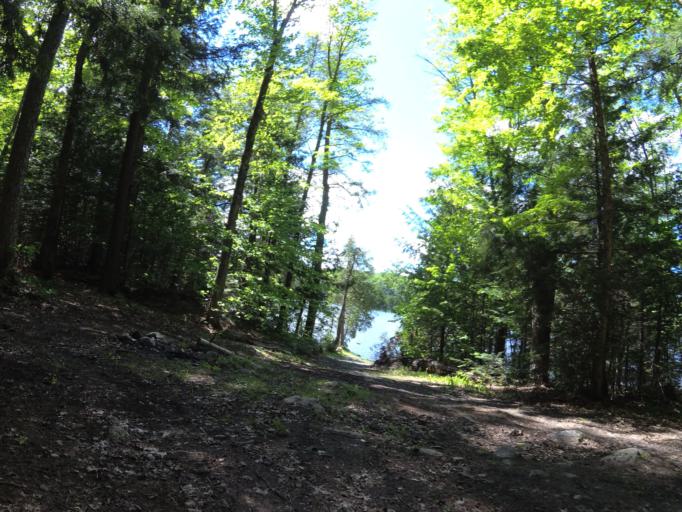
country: CA
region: Ontario
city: Renfrew
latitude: 45.0490
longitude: -76.8368
